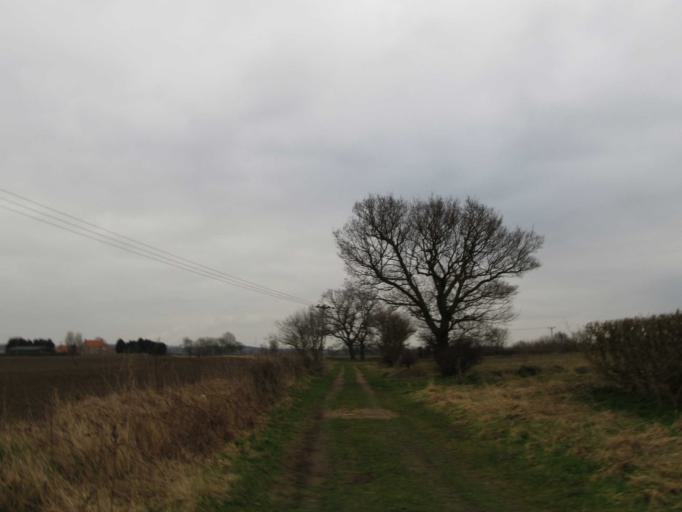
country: GB
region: England
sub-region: Doncaster
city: Bawtry
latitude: 53.4289
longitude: -0.9653
